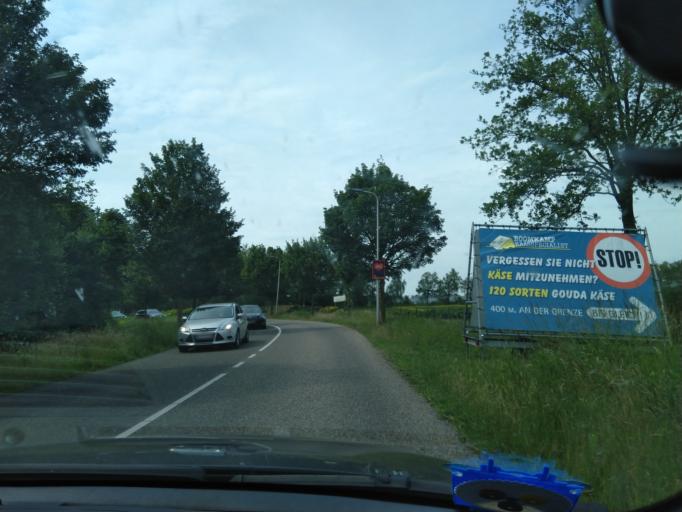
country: DE
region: Lower Saxony
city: Nordhorn
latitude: 52.3993
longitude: 7.0283
